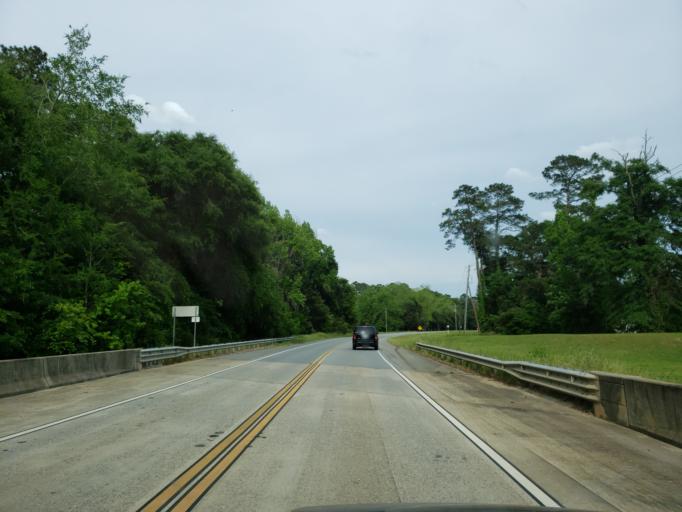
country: US
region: Georgia
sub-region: Dooly County
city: Vienna
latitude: 32.1115
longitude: -83.8361
